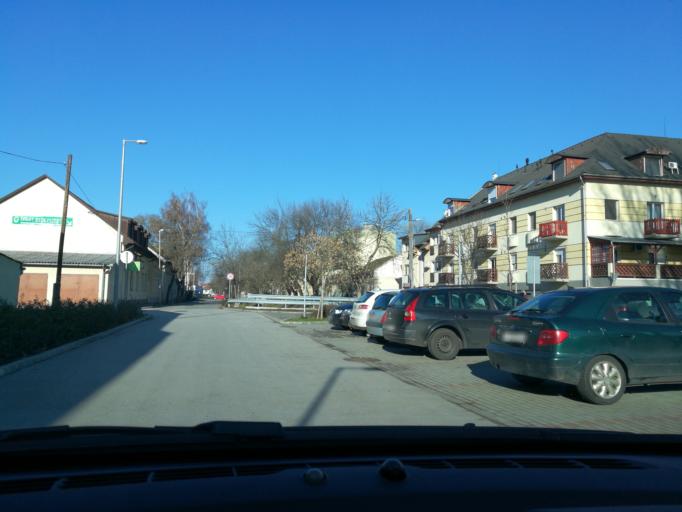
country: HU
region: Szabolcs-Szatmar-Bereg
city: Nyiregyhaza
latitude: 47.9452
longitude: 21.7114
